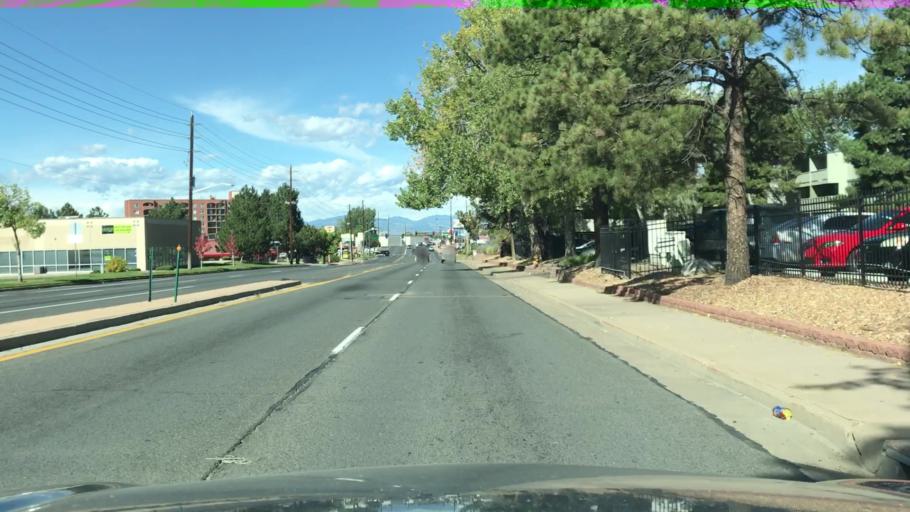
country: US
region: Colorado
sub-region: Arapahoe County
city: Glendale
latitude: 39.6992
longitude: -104.9053
